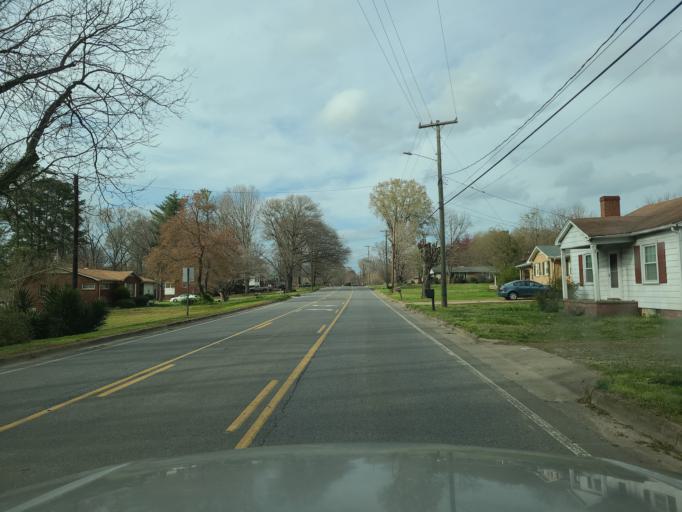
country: US
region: North Carolina
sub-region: Cleveland County
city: Shelby
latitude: 35.2788
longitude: -81.5625
